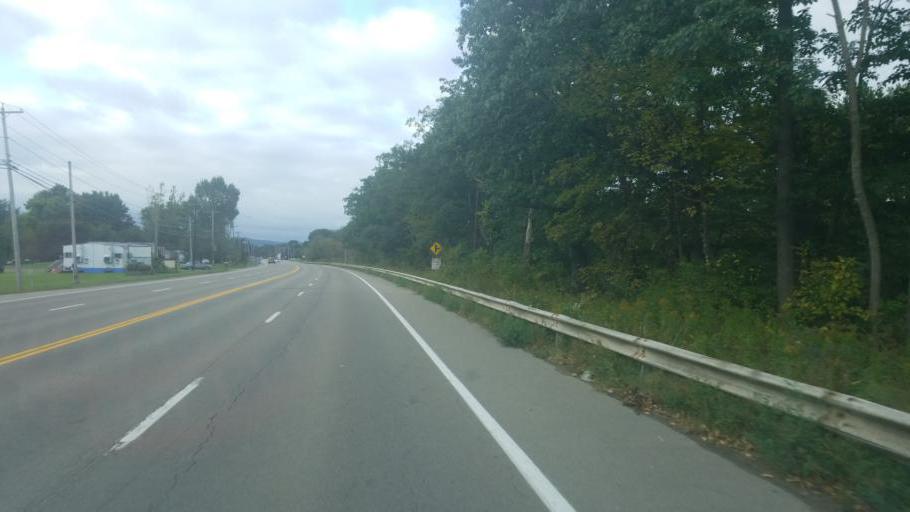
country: US
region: New York
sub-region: Cattaraugus County
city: Olean
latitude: 42.1311
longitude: -78.4087
